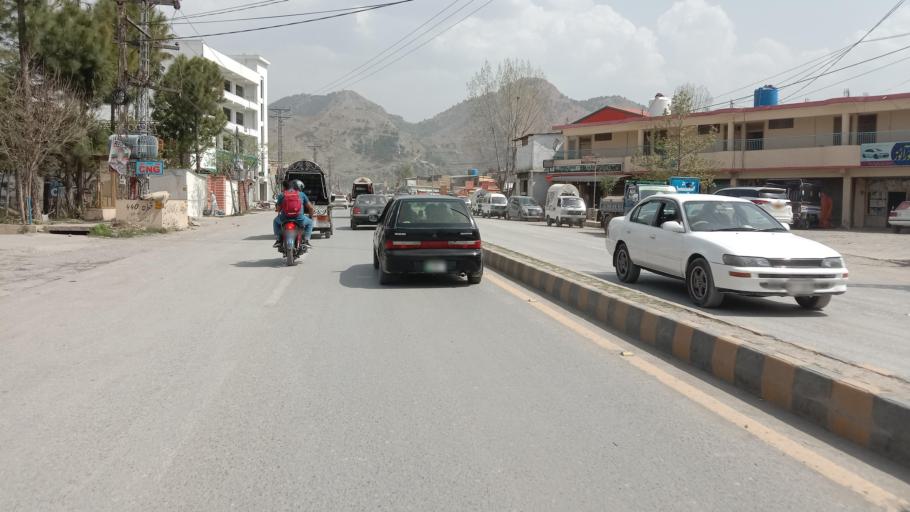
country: PK
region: Khyber Pakhtunkhwa
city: Abbottabad
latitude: 34.1579
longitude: 73.2539
